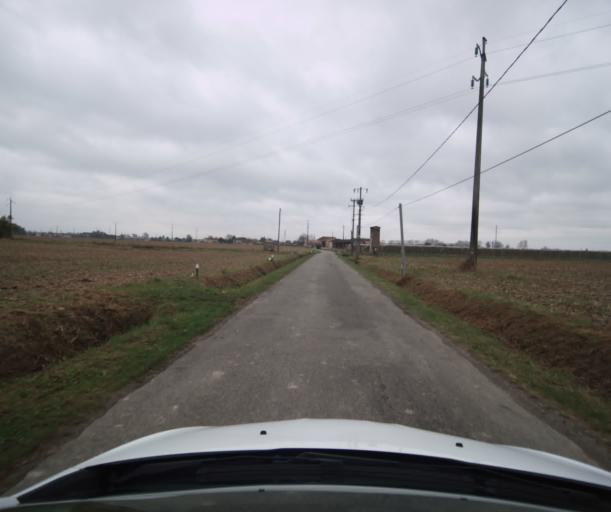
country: FR
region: Midi-Pyrenees
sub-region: Departement du Tarn-et-Garonne
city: Castelsarrasin
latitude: 44.0477
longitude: 1.1293
